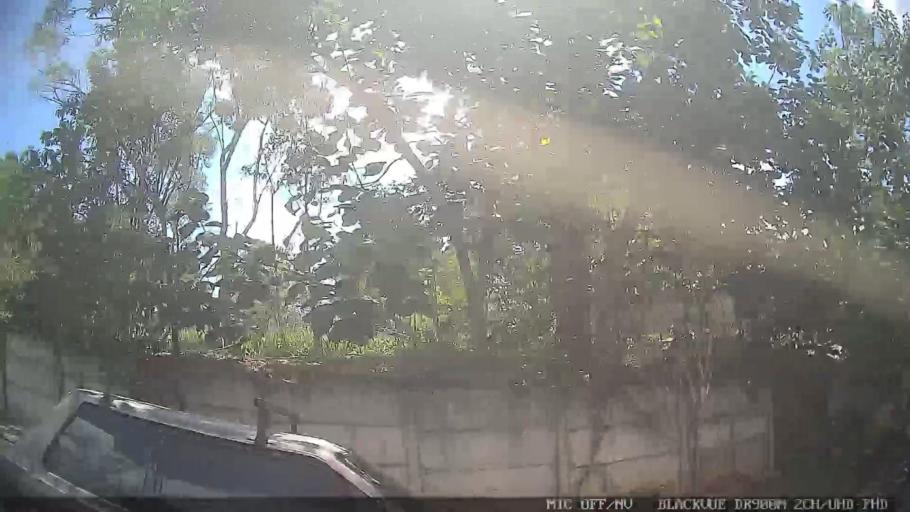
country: BR
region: Sao Paulo
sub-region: Atibaia
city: Atibaia
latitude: -23.1230
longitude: -46.6028
